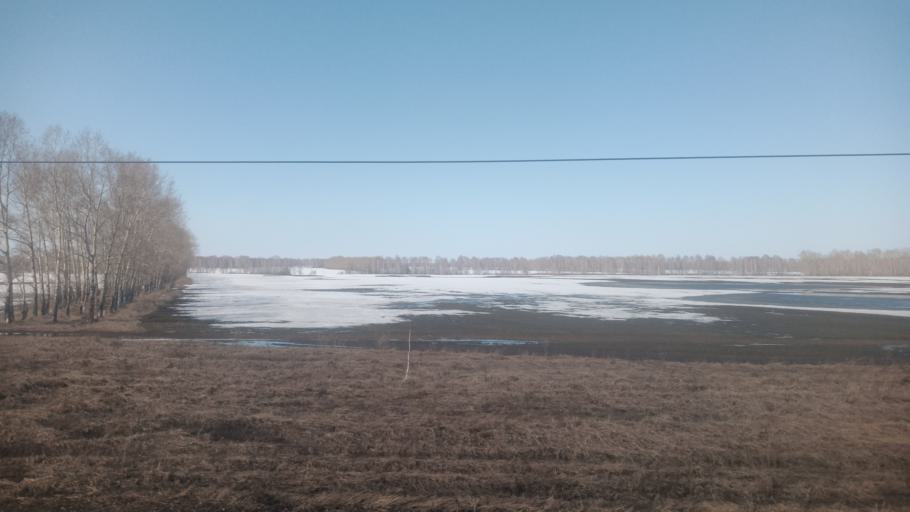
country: RU
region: Altai Krai
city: Logovskoye
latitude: 53.4845
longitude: 84.1485
